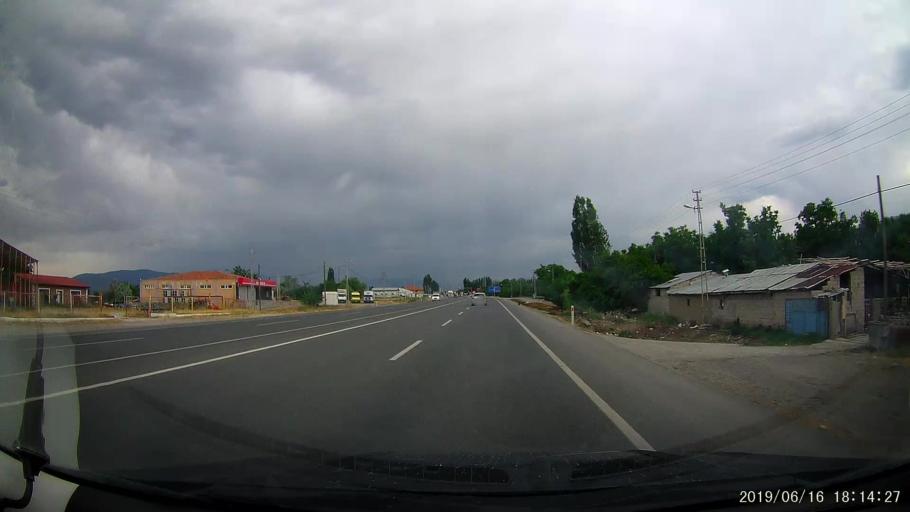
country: TR
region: Erzincan
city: Erzincan
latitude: 39.7240
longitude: 39.5581
